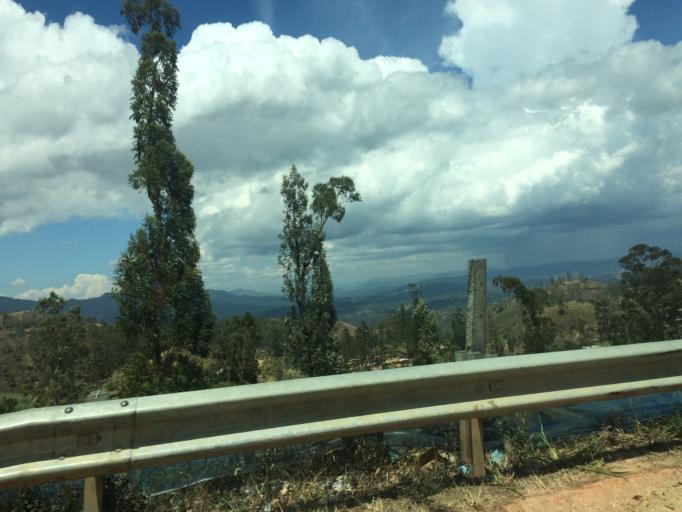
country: LK
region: Central
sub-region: Nuwara Eliya District
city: Nuwara Eliya
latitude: 6.9083
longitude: 80.8380
